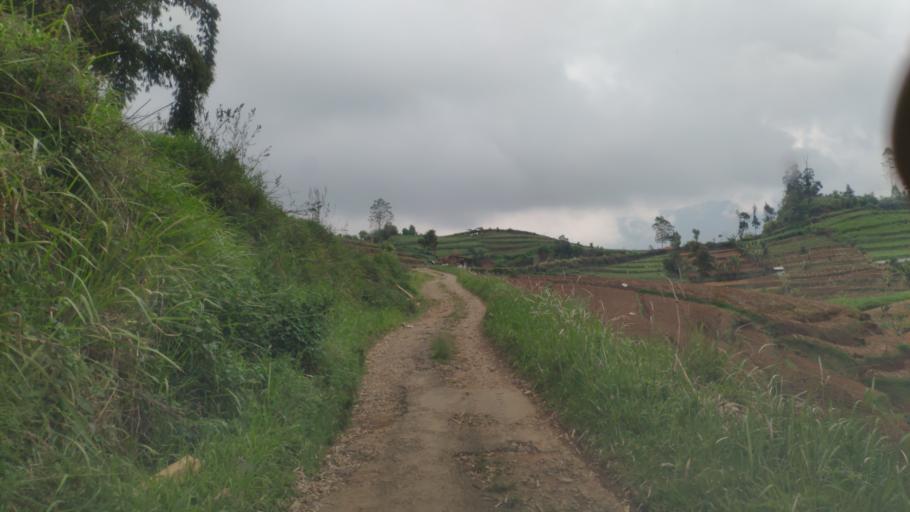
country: ID
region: Central Java
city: Wonosobo
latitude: -7.2258
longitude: 109.7845
